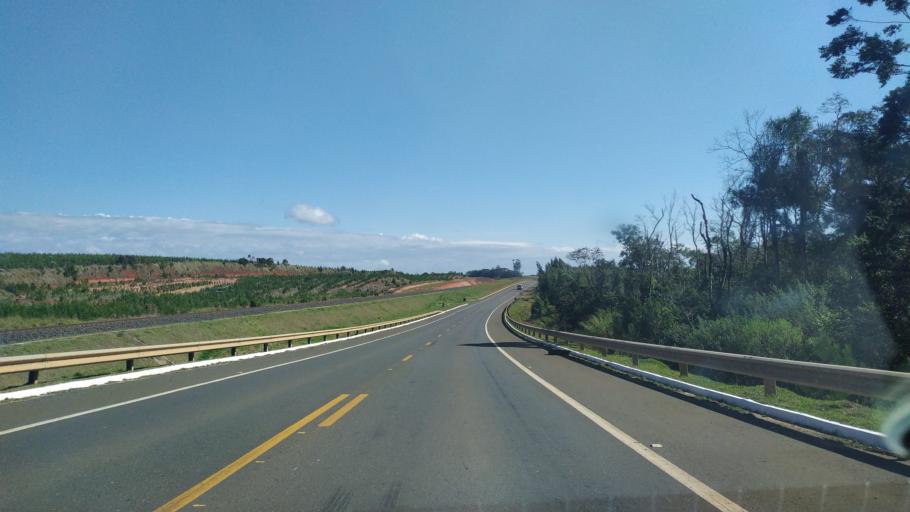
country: BR
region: Parana
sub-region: Ortigueira
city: Ortigueira
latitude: -24.2569
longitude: -50.7885
